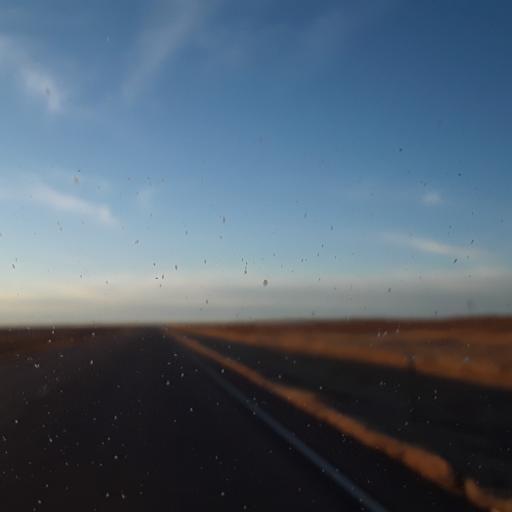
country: US
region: Colorado
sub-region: Cheyenne County
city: Cheyenne Wells
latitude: 38.8129
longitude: -102.4710
